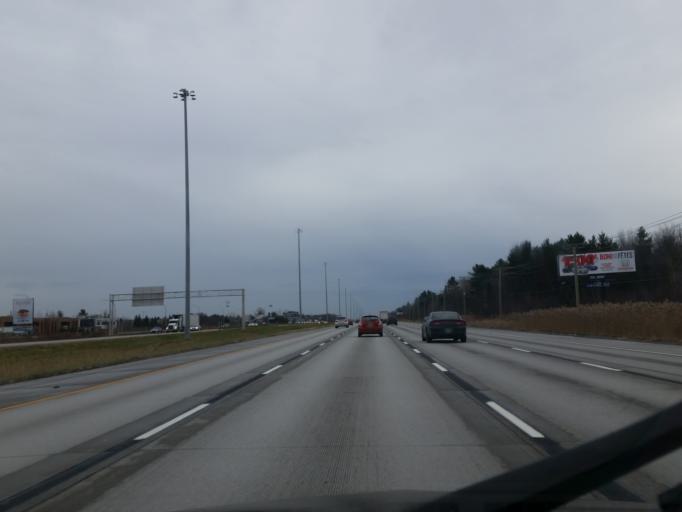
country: CA
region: Quebec
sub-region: Laurentides
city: Blainville
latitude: 45.6676
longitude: -73.9006
